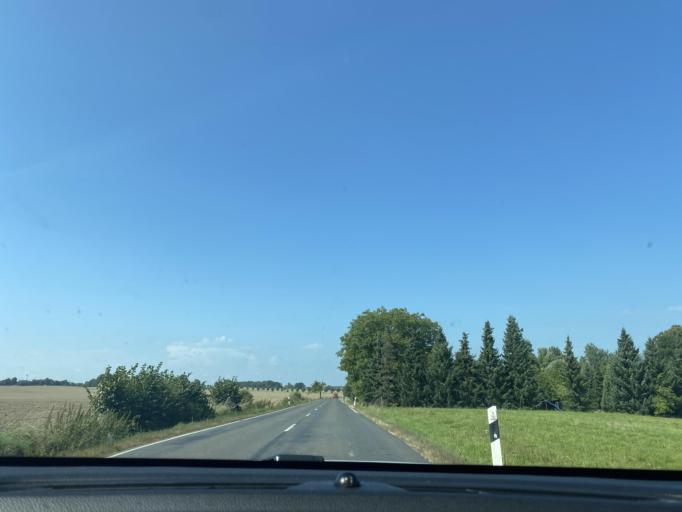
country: DE
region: Saxony
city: Reichenbach
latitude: 51.1713
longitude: 14.7786
